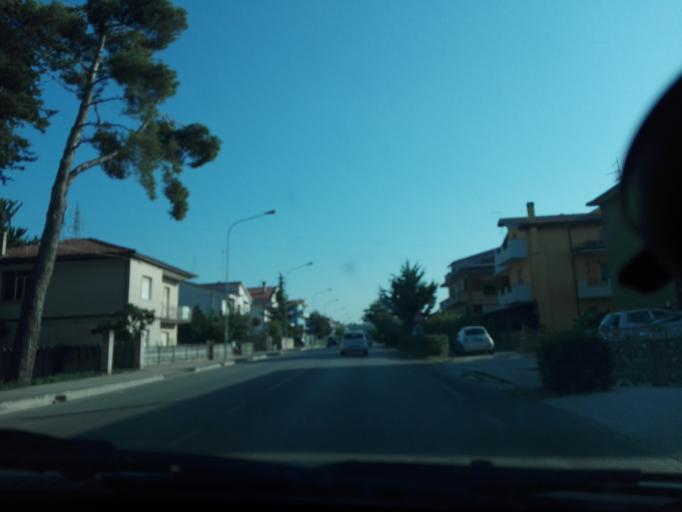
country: IT
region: Abruzzo
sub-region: Provincia di Pescara
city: Cappelle sul Tavo
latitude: 42.4873
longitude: 14.1200
